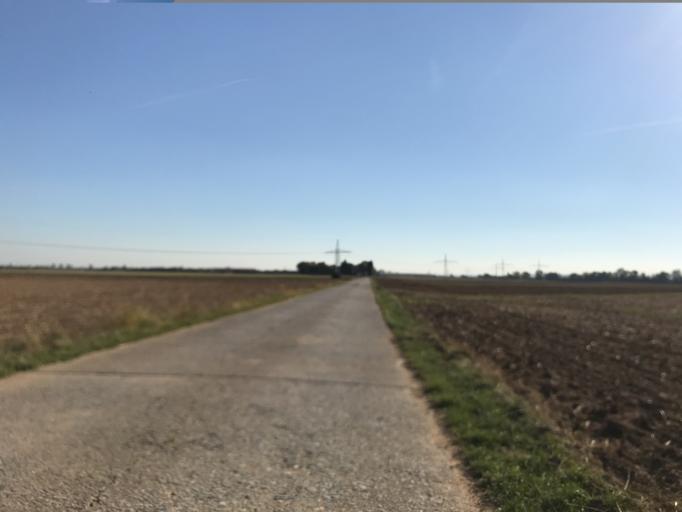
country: DE
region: Hesse
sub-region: Regierungsbezirk Darmstadt
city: Hochheim am Main
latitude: 50.0468
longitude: 8.3390
